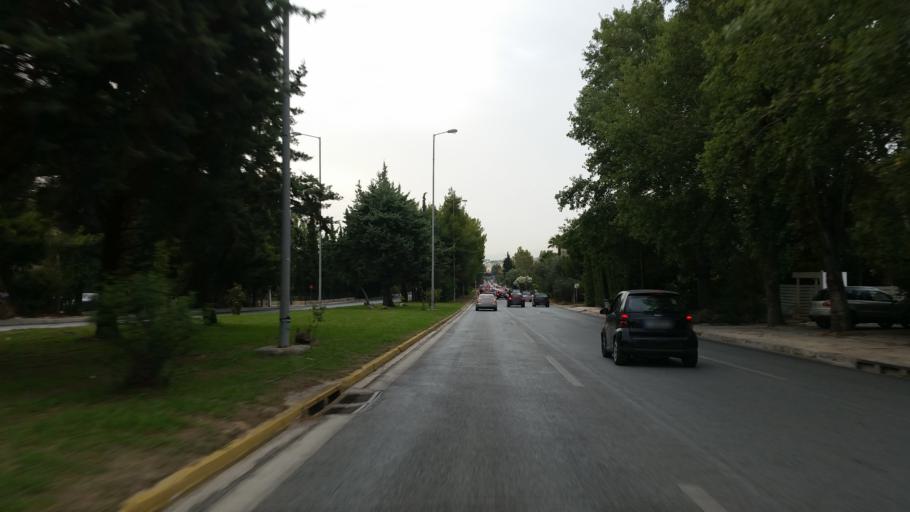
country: GR
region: Attica
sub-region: Nomarchia Anatolikis Attikis
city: Vouliagmeni
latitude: 37.8253
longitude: 23.7747
